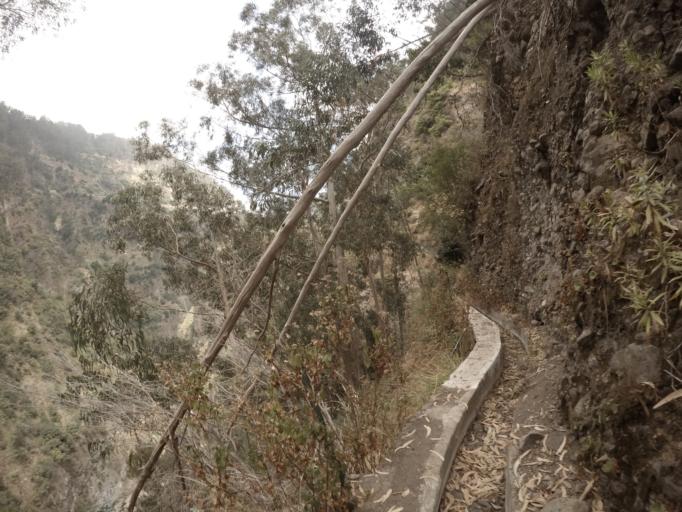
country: PT
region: Madeira
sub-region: Camara de Lobos
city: Curral das Freiras
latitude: 32.6850
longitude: -16.9623
